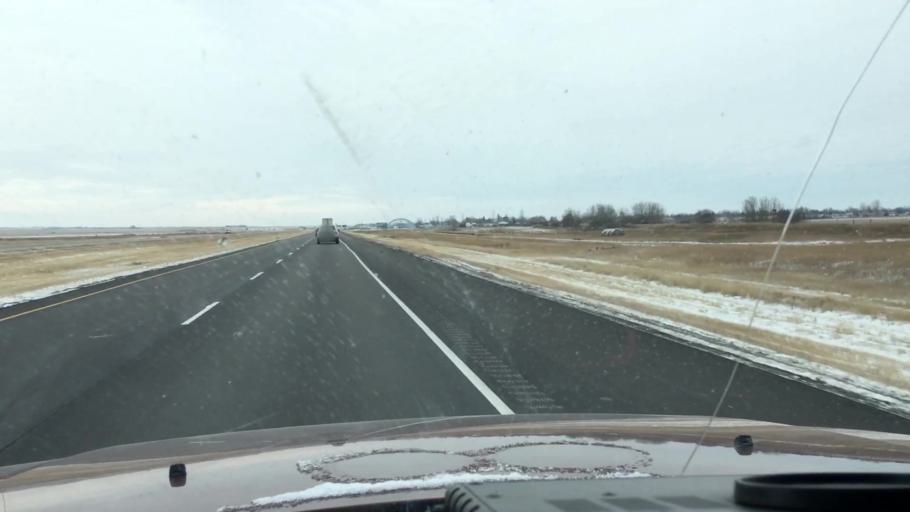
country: CA
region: Saskatchewan
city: Saskatoon
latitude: 51.8241
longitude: -106.5004
